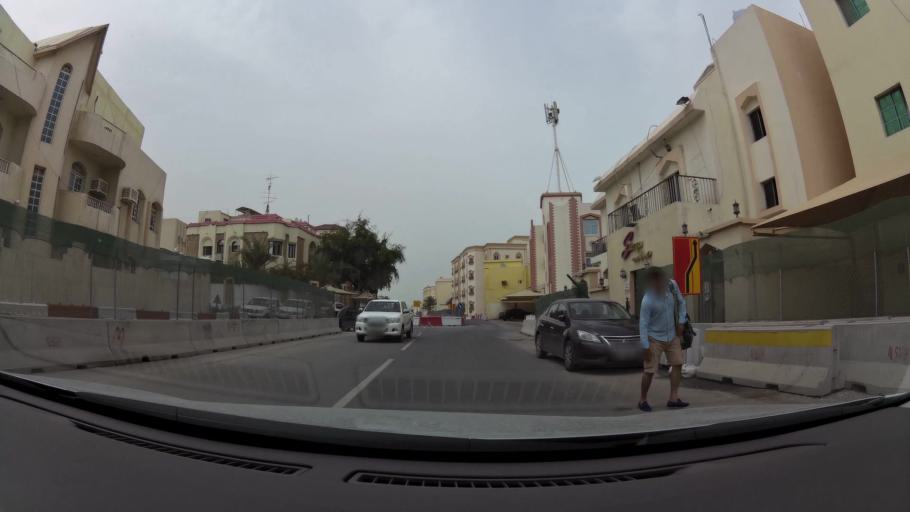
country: QA
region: Baladiyat ad Dawhah
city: Doha
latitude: 25.2540
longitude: 51.5566
